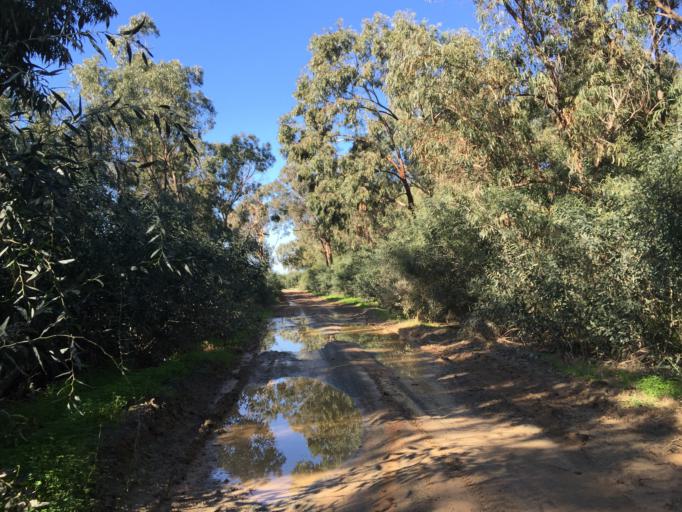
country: CY
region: Limassol
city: Ypsonas
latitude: 34.6423
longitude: 32.9922
